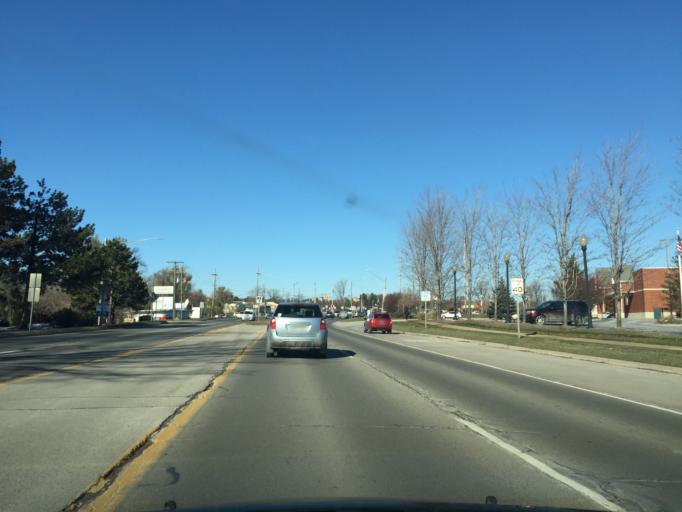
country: US
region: Michigan
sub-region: Oakland County
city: Lake Orion
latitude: 42.7877
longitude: -83.2449
